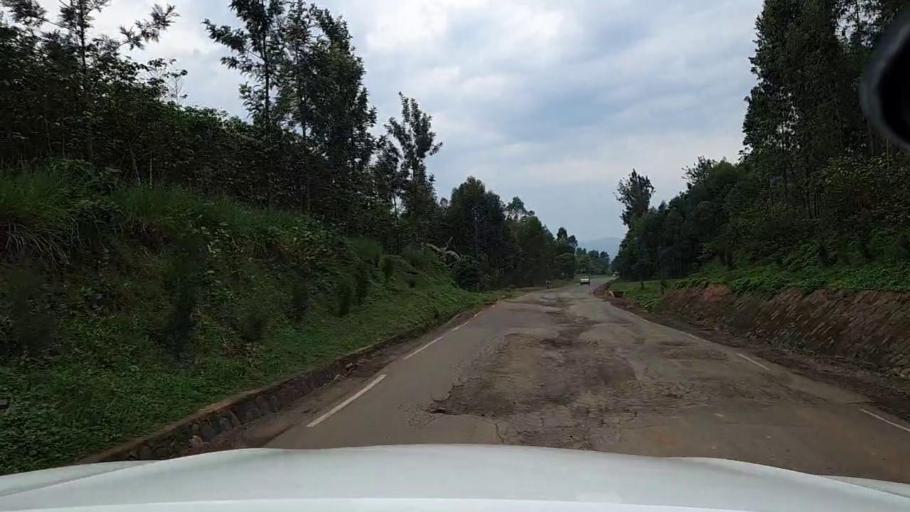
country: RW
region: Western Province
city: Cyangugu
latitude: -2.6542
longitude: 28.9703
